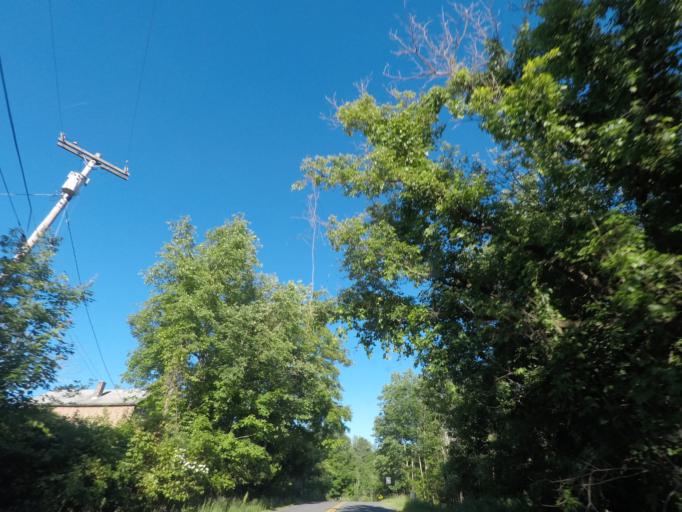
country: US
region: New York
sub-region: Rensselaer County
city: Averill Park
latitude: 42.5823
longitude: -73.5515
